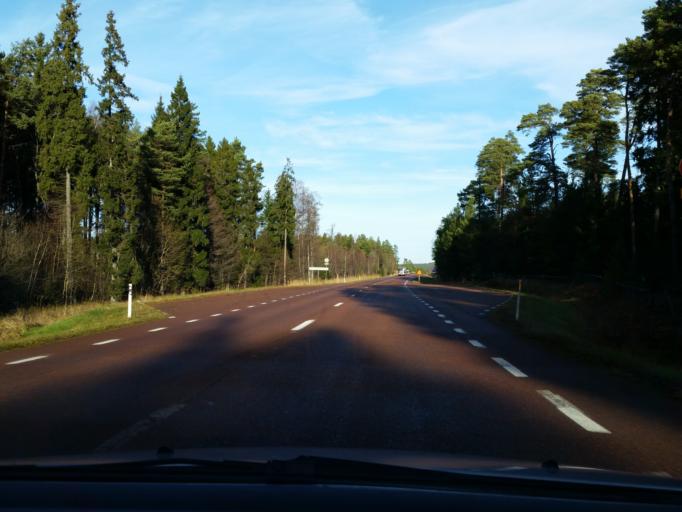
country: AX
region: Alands landsbygd
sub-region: Finstroem
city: Finstroem
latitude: 60.2826
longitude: 19.9528
